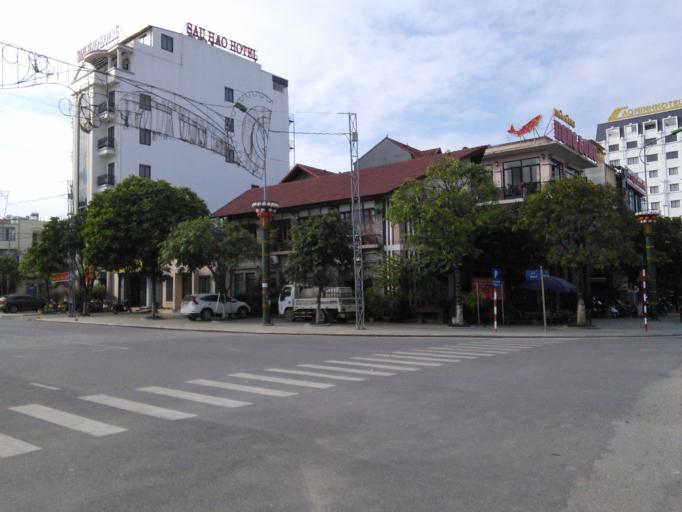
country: VN
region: Lao Cai
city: Lao Cai
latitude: 22.4919
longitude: 103.9702
